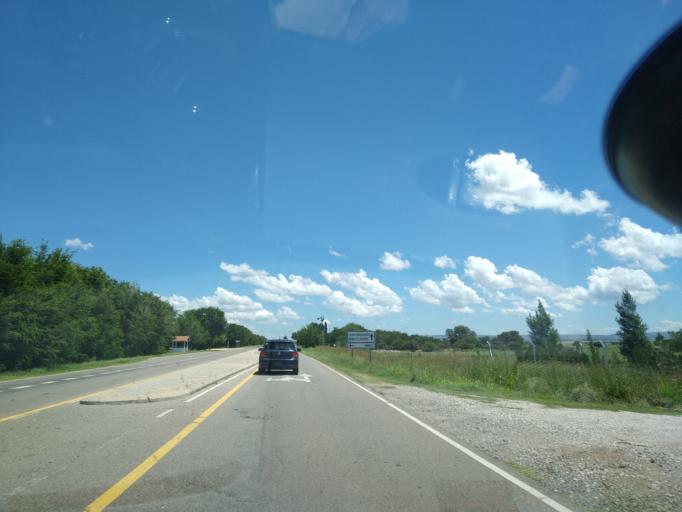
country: AR
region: Cordoba
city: Salsacate
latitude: -31.4961
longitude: -65.1085
